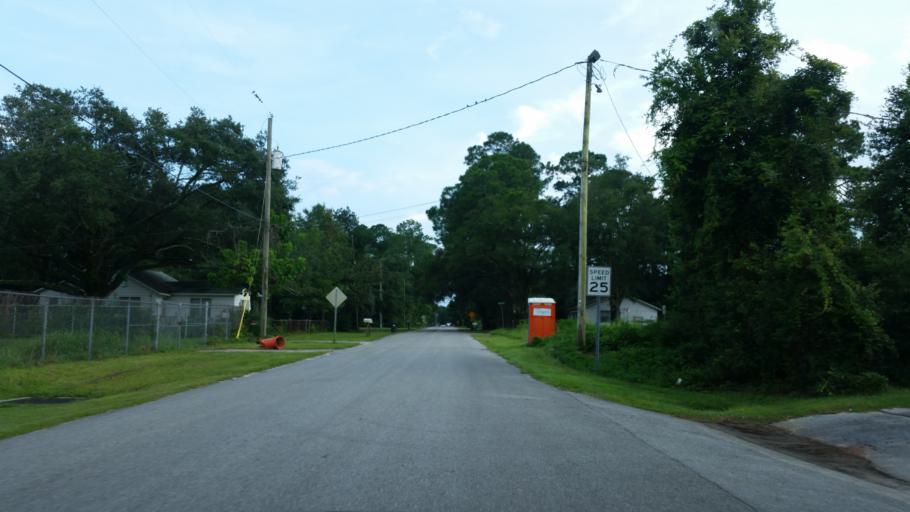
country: US
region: Florida
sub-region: Escambia County
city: Ferry Pass
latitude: 30.5154
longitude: -87.2127
